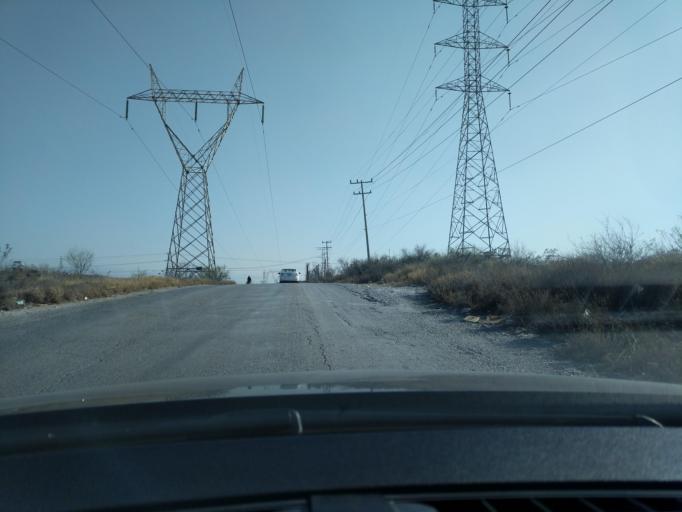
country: MX
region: Coahuila
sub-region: Ramos Arizpe
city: Ramos Arizpe
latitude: 25.5363
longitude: -100.9781
